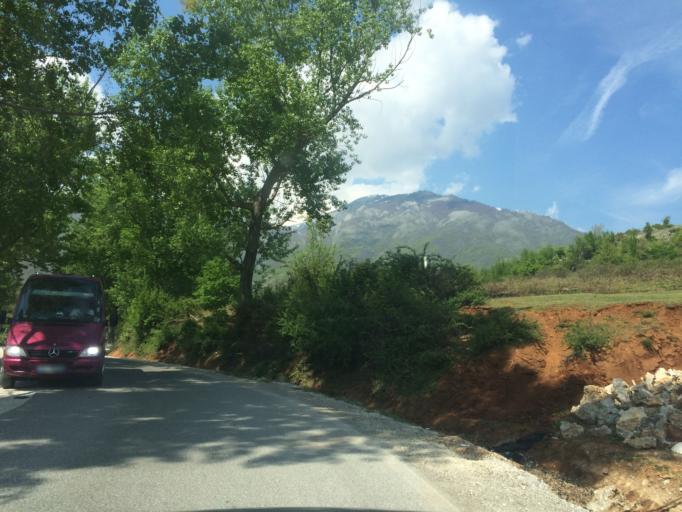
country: AL
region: Kukes
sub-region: Rrethi i Tropojes
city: Bajram Curri
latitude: 42.3572
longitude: 20.0909
